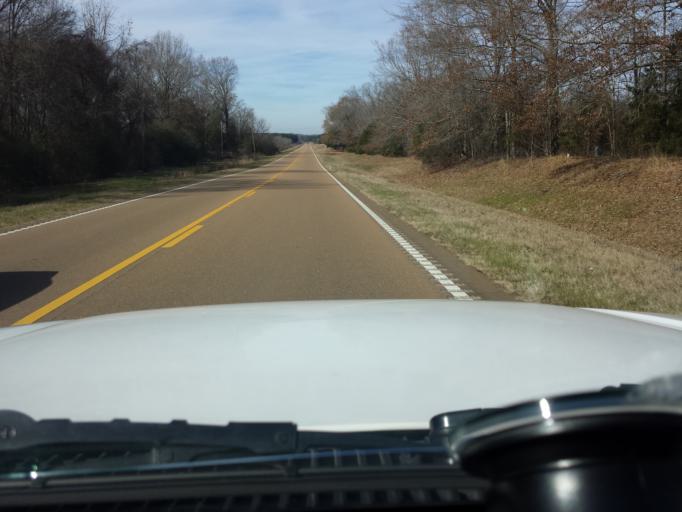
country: US
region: Mississippi
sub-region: Madison County
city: Canton
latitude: 32.6931
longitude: -90.0697
